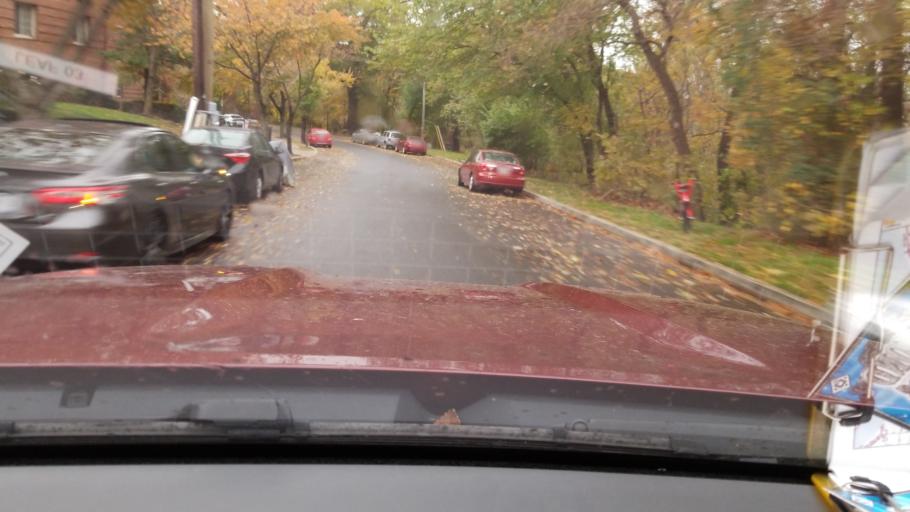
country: US
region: Maryland
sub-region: Prince George's County
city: Glassmanor
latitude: 38.8463
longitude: -77.0044
